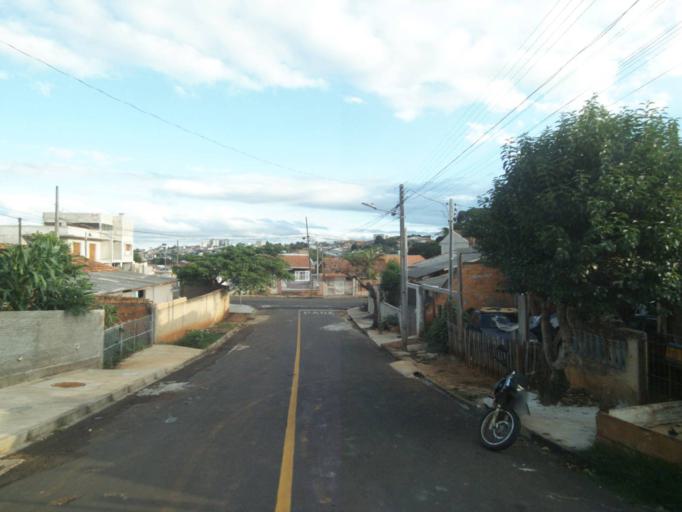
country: BR
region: Parana
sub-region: Telemaco Borba
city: Telemaco Borba
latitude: -24.3247
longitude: -50.6384
